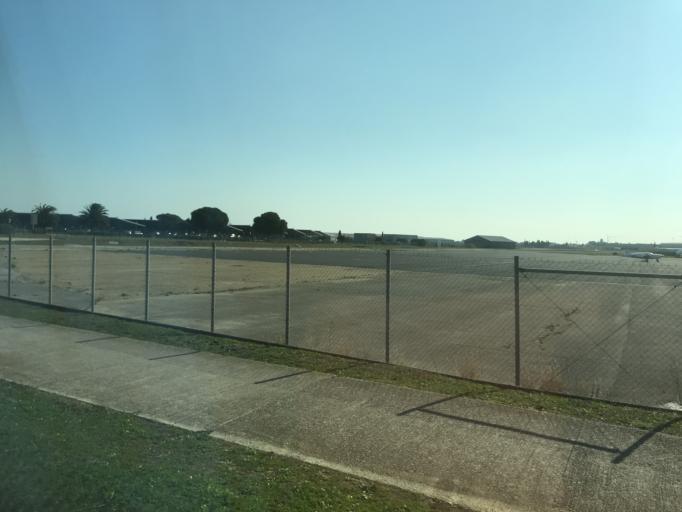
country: FR
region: Languedoc-Roussillon
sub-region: Departement de l'Herault
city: Perols
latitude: 43.5795
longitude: 3.9541
